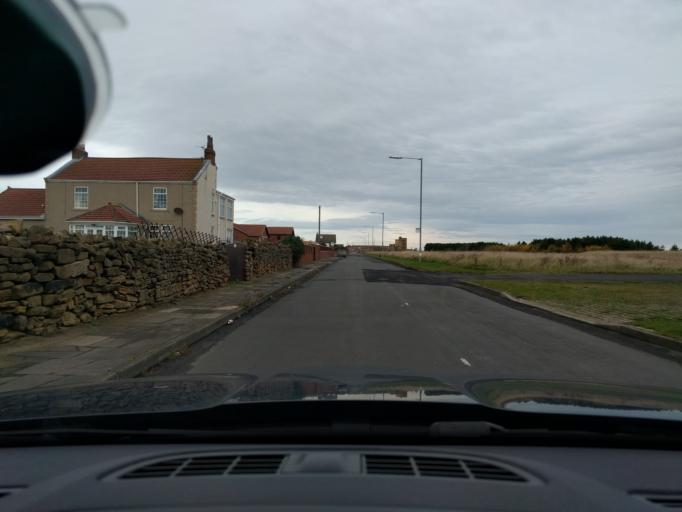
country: GB
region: England
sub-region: Northumberland
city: Blyth
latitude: 55.1512
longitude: -1.5239
